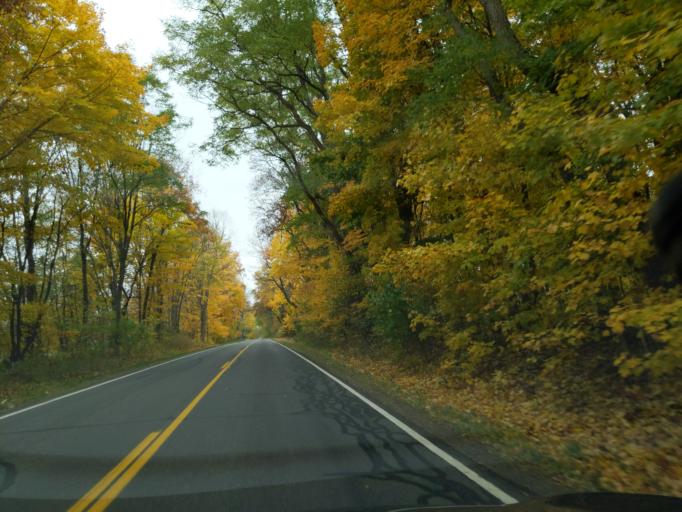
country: US
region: Michigan
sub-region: Eaton County
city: Eaton Rapids
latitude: 42.3767
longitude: -84.6005
